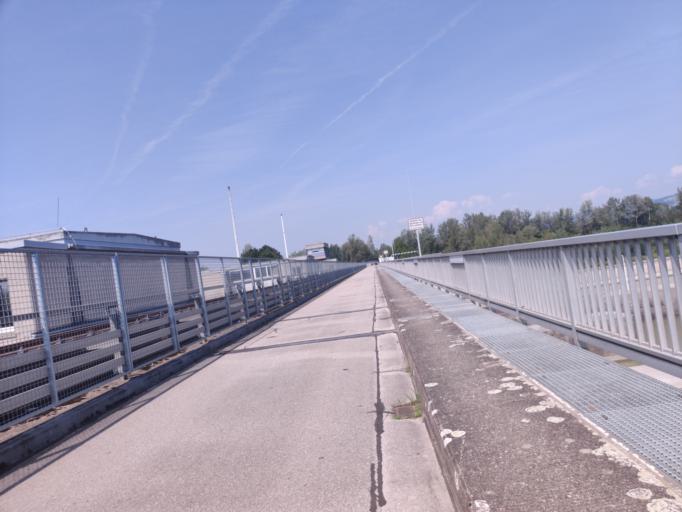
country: AT
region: Upper Austria
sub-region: Politischer Bezirk Urfahr-Umgebung
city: Ottensheim
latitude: 48.3178
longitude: 14.1503
